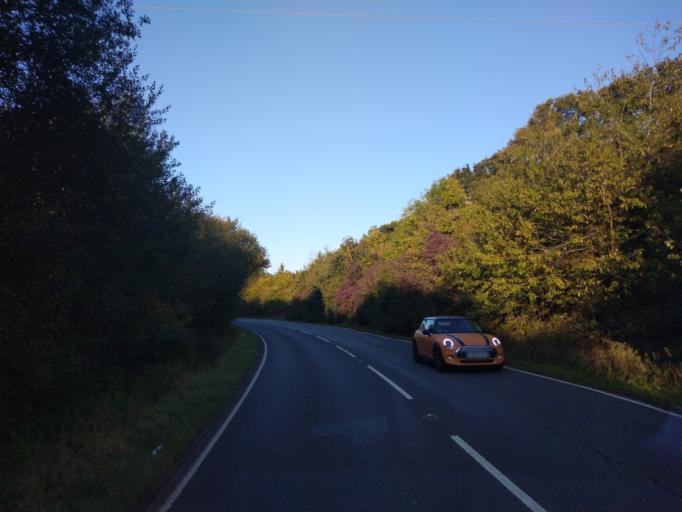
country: GB
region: England
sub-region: West Sussex
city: Goring-by-Sea
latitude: 50.8388
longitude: -0.4466
